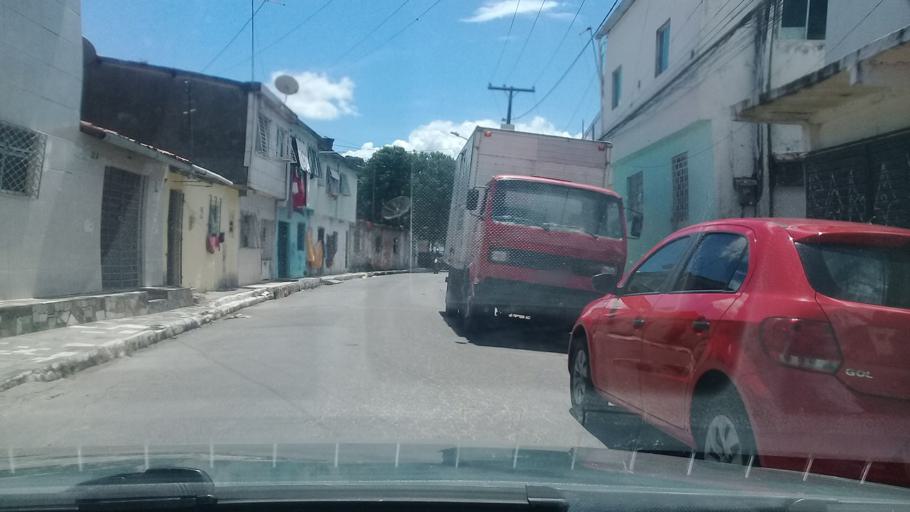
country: BR
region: Pernambuco
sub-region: Jaboatao Dos Guararapes
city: Jaboatao dos Guararapes
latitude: -8.1270
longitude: -34.9495
